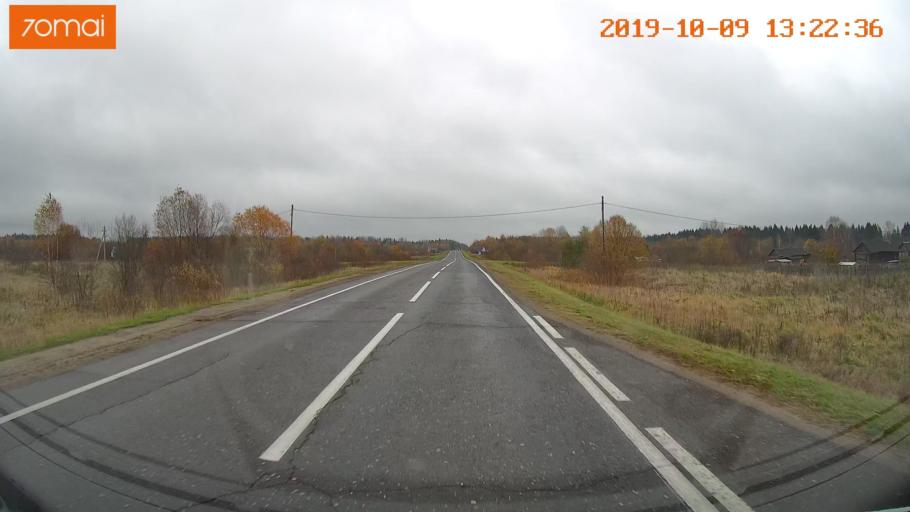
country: RU
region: Jaroslavl
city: Lyubim
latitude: 58.3393
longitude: 40.8688
